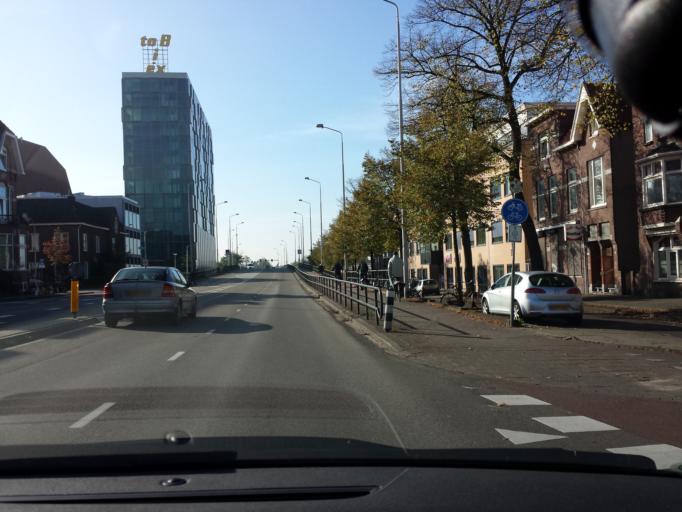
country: NL
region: Gelderland
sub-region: Gemeente Nijmegen
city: Nijmegen
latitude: 51.8399
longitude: 5.8541
